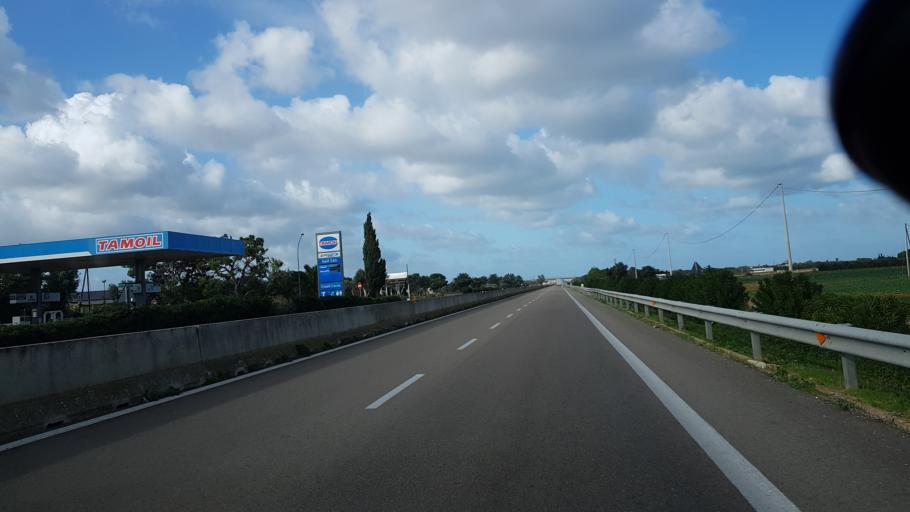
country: IT
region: Apulia
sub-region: Provincia di Brindisi
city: Carovigno
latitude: 40.7358
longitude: 17.7257
